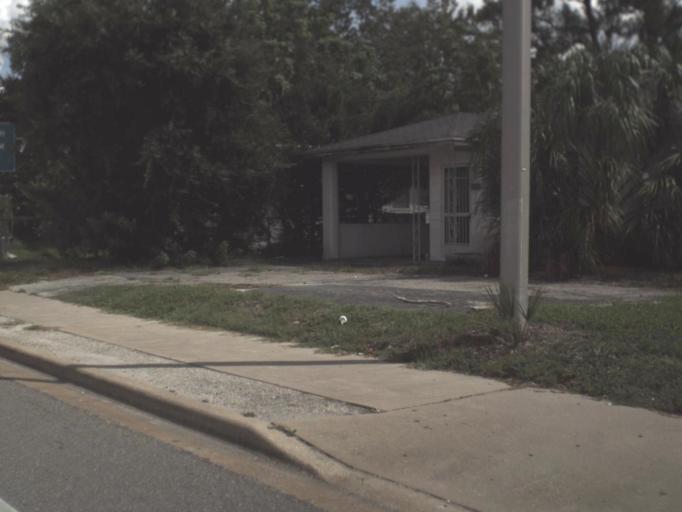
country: US
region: Florida
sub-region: Sarasota County
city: Sarasota
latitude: 27.3374
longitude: -82.5153
